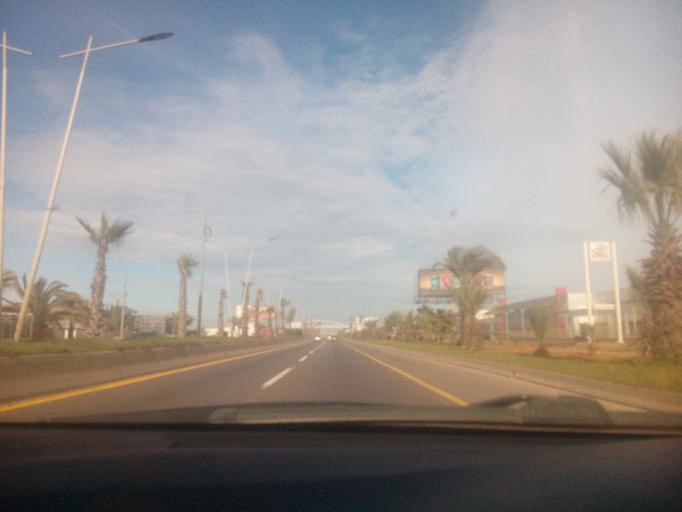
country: DZ
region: Oran
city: Es Senia
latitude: 35.6364
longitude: -0.5881
